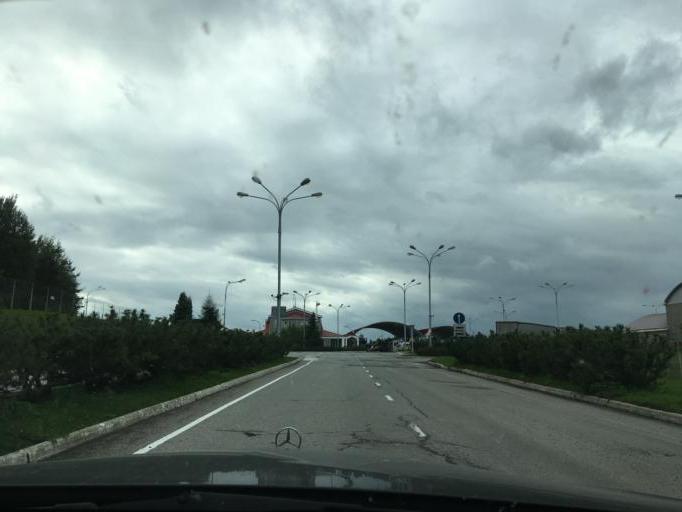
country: RU
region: Pskov
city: Pechory
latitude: 57.6450
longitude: 27.3902
